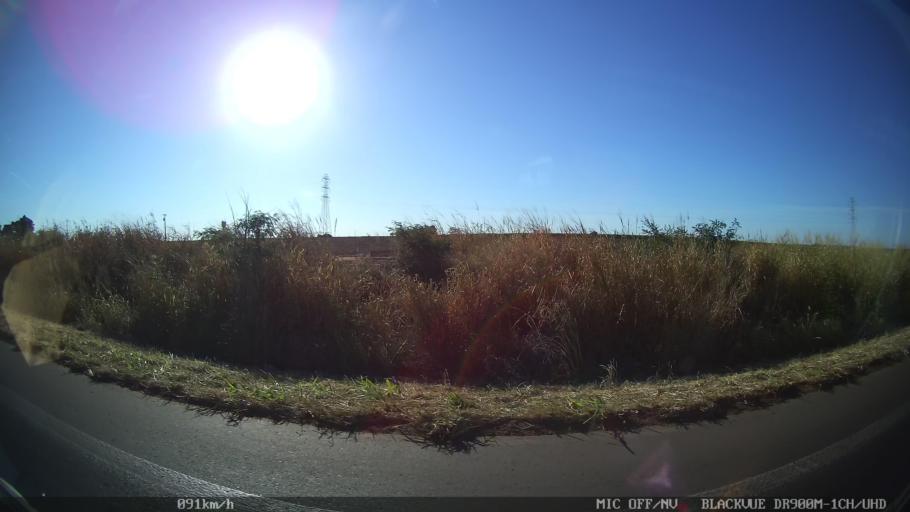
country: BR
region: Sao Paulo
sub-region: Olimpia
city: Olimpia
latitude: -20.6989
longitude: -48.9353
